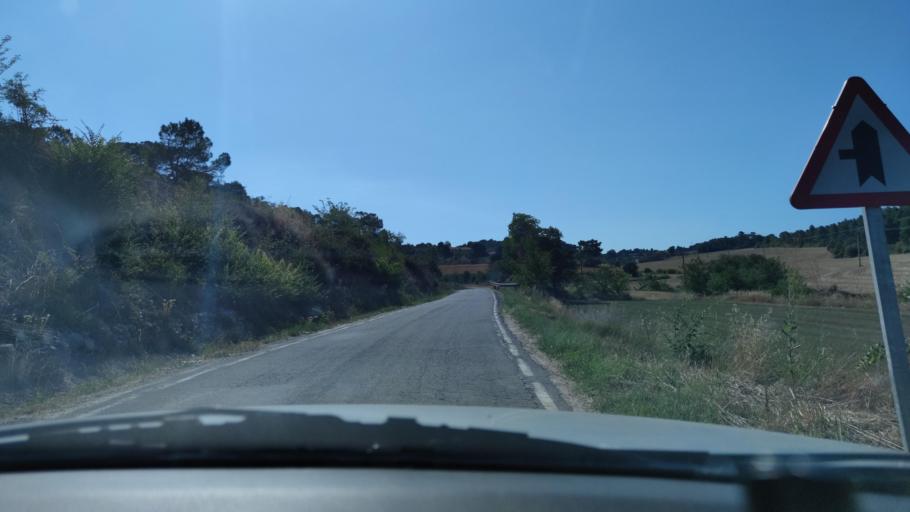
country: ES
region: Catalonia
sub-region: Provincia de Lleida
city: Sant Guim de Freixenet
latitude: 41.6866
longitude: 1.3941
